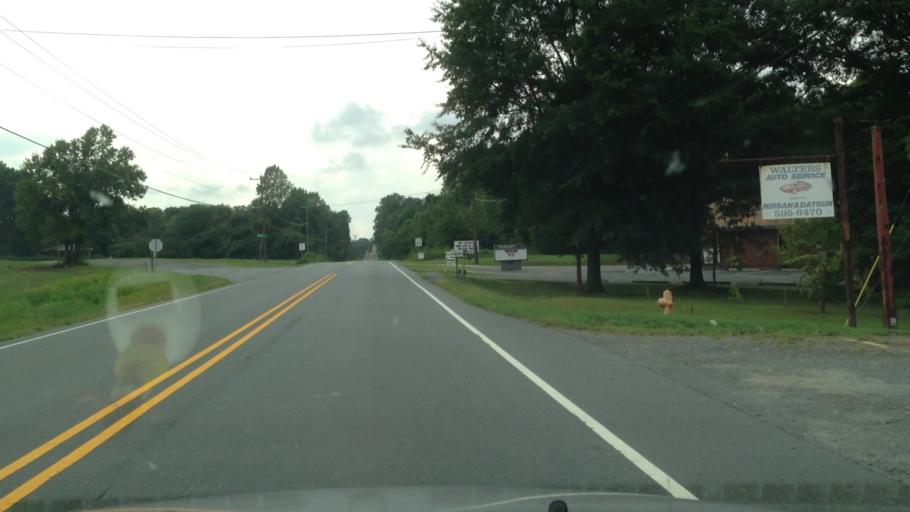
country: US
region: North Carolina
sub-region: Forsyth County
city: Walkertown
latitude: 36.1569
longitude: -80.1302
